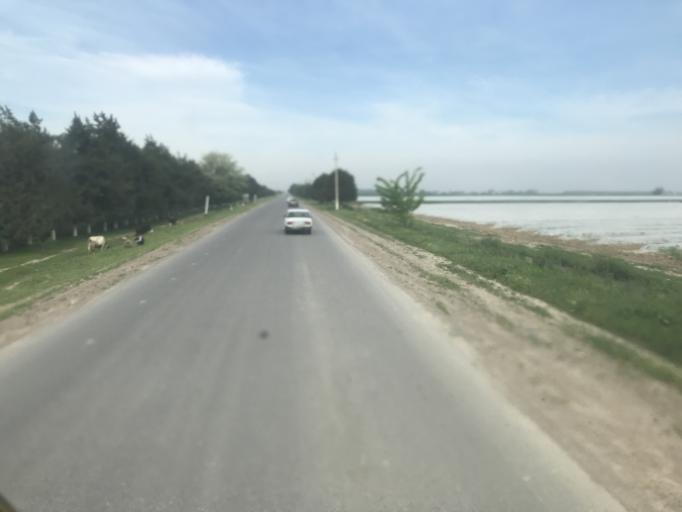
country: KZ
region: Ongtustik Qazaqstan
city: Asykata
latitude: 40.9845
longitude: 68.2954
